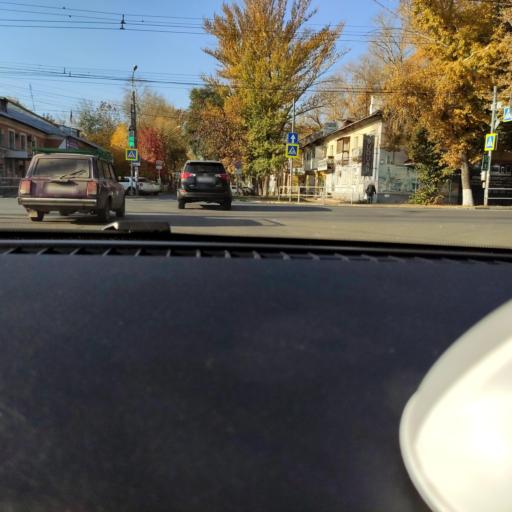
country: RU
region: Samara
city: Samara
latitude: 53.2224
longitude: 50.2589
